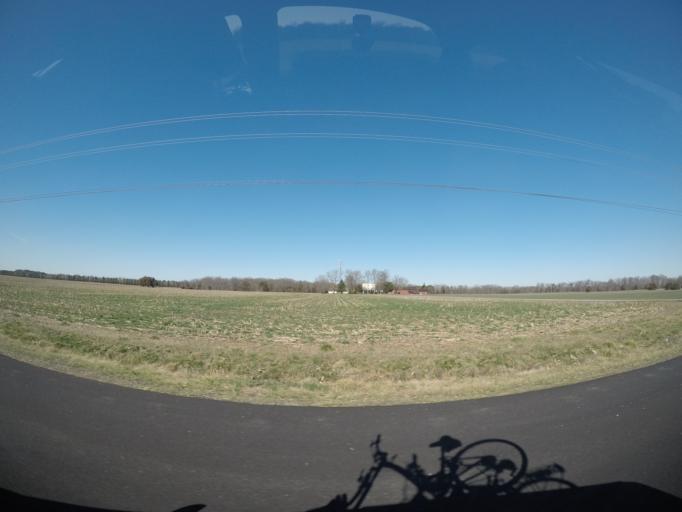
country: US
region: Delaware
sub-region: New Castle County
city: Townsend
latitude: 39.3607
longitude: -75.8278
